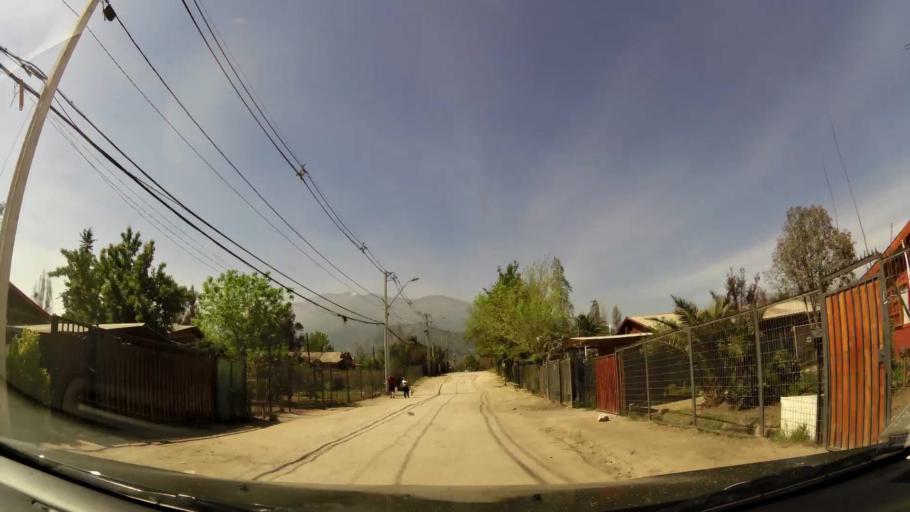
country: CL
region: Santiago Metropolitan
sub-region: Provincia de Cordillera
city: Puente Alto
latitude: -33.5728
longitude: -70.5584
